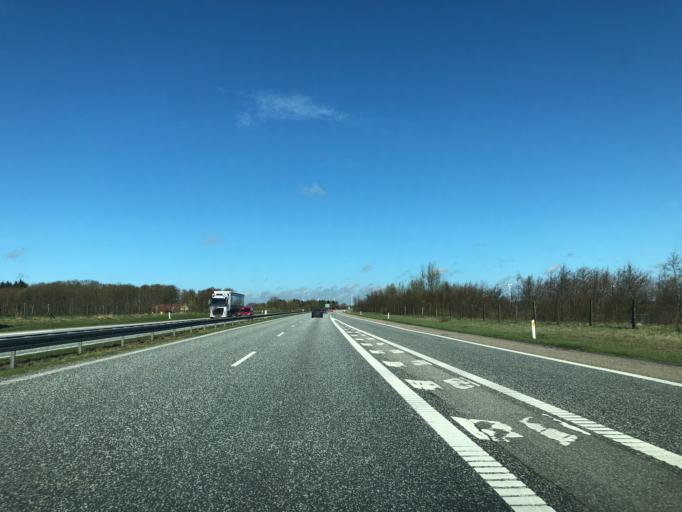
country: DK
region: North Denmark
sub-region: Bronderslev Kommune
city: Bronderslev
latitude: 57.2074
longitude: 9.9322
